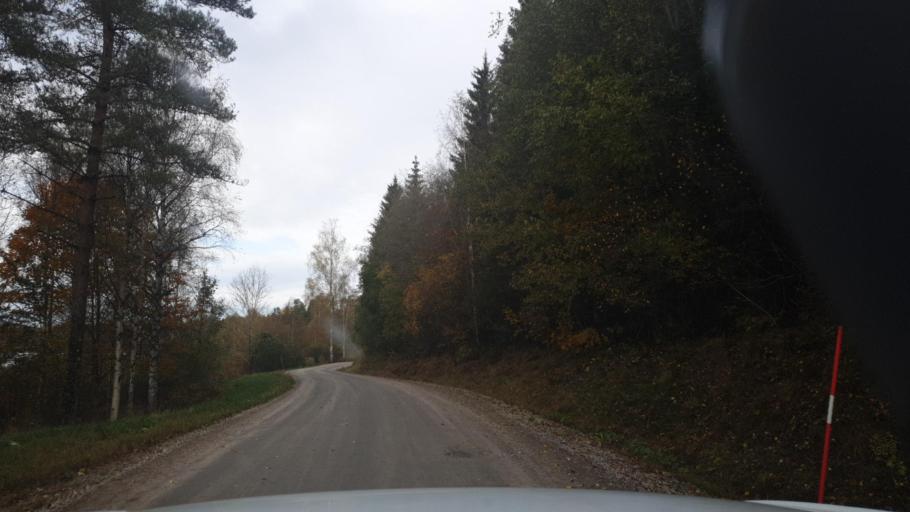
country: SE
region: Vaermland
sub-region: Arvika Kommun
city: Arvika
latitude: 59.7077
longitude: 12.8540
